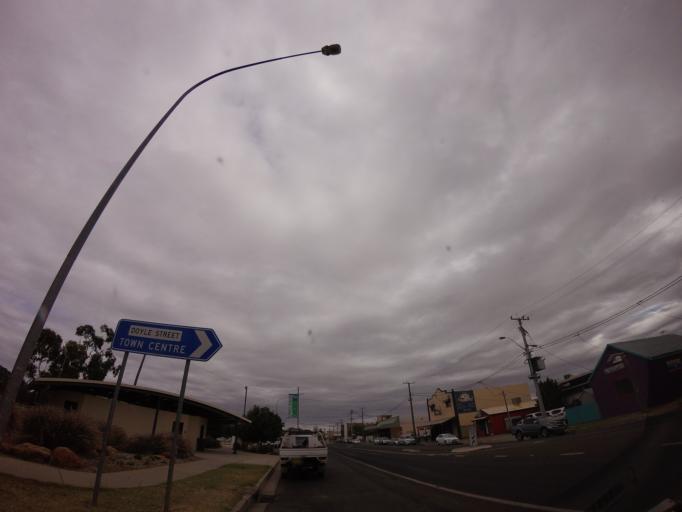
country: AU
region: New South Wales
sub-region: Narrabri
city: Narrabri
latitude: -30.3252
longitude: 149.7820
